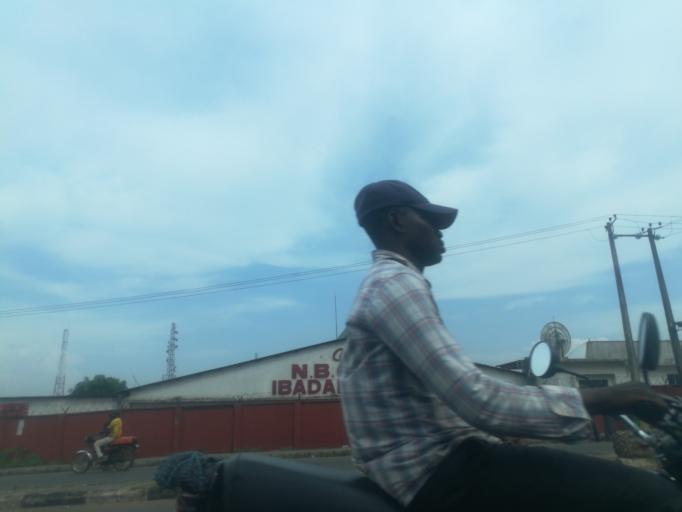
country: NG
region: Oyo
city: Ibadan
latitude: 7.4151
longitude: 3.8950
